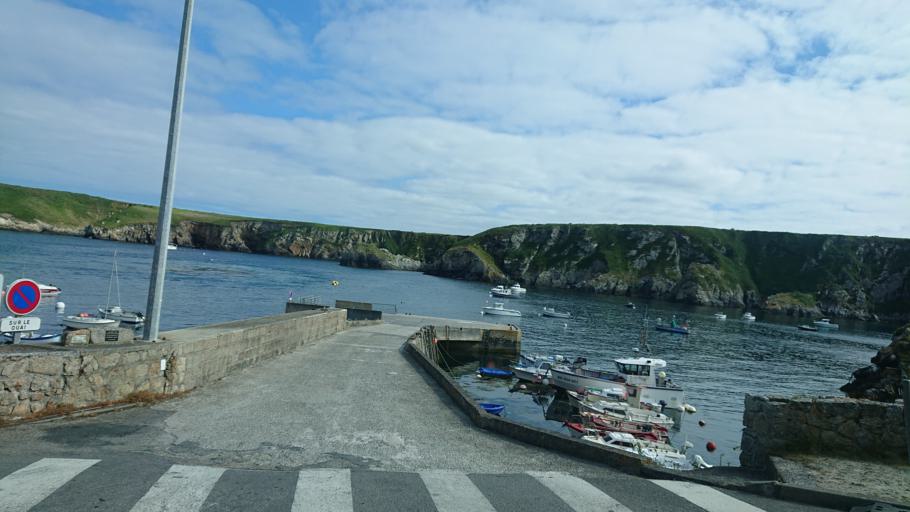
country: FR
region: Brittany
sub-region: Departement du Finistere
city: Porspoder
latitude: 48.4696
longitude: -5.0558
